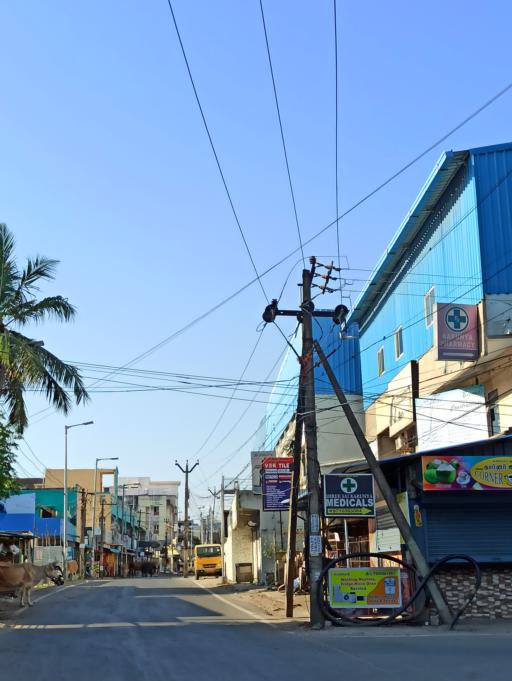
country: IN
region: Tamil Nadu
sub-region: Kancheepuram
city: Manappakkam
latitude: 13.0228
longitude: 80.1674
